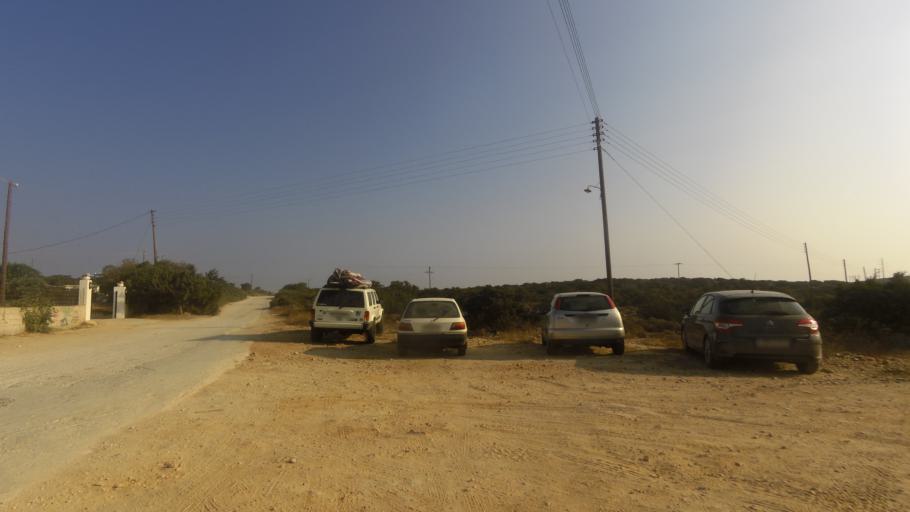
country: GR
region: South Aegean
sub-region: Nomos Kykladon
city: Antiparos
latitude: 37.0438
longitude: 25.0838
